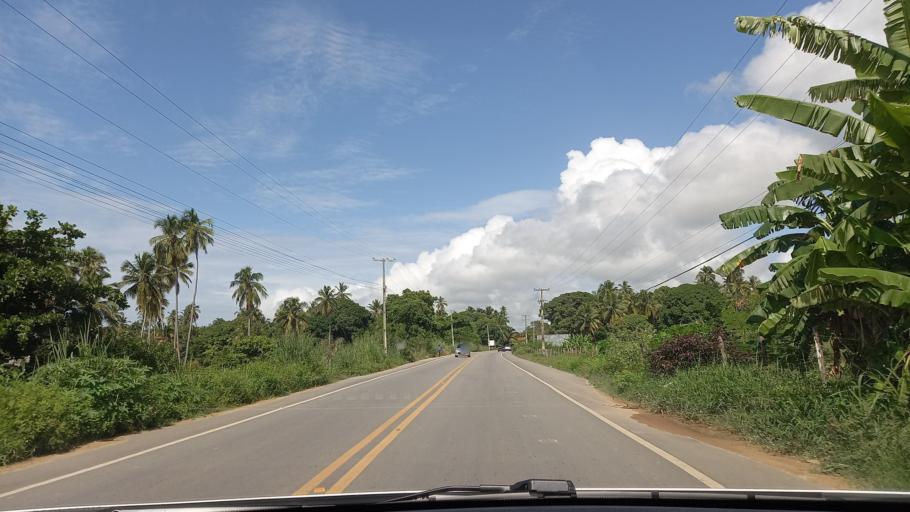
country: BR
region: Alagoas
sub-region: Maragogi
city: Maragogi
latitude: -8.9892
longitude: -35.2012
